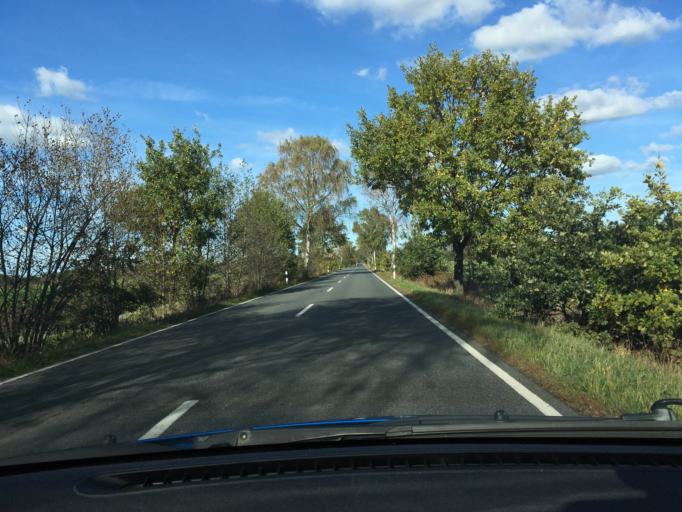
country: DE
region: Lower Saxony
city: Isernhagen Farster Bauerschaft
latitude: 52.5515
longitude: 9.8543
